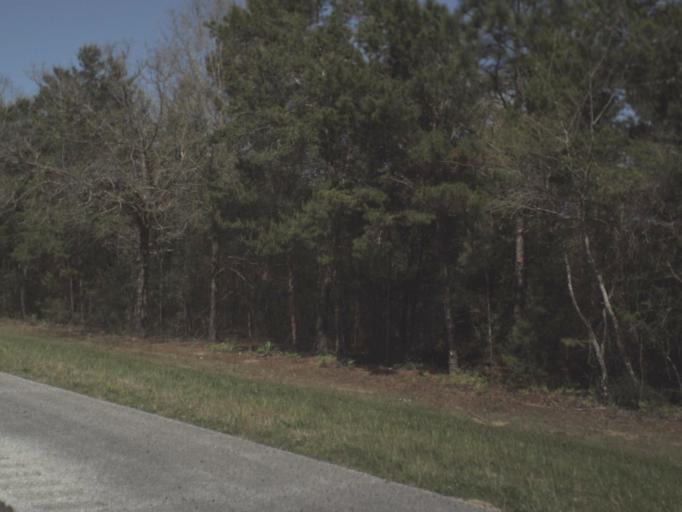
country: US
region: Florida
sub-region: Okaloosa County
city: Crestview
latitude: 30.7341
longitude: -86.3734
